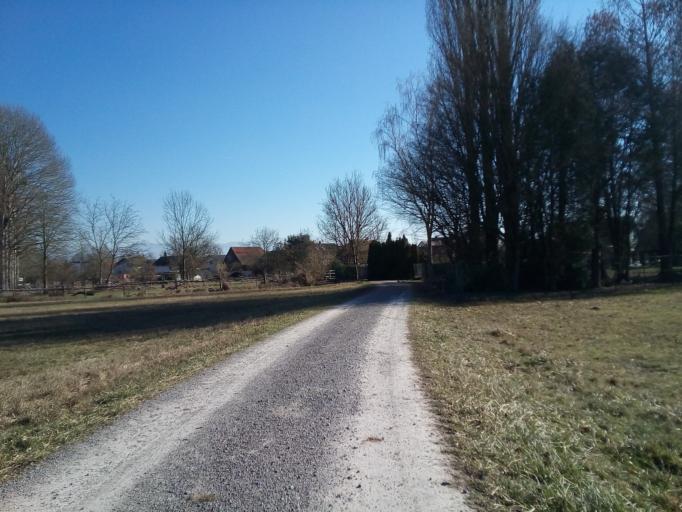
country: DE
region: Baden-Wuerttemberg
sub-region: Karlsruhe Region
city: Schwarzach
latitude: 48.7362
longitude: 8.0562
